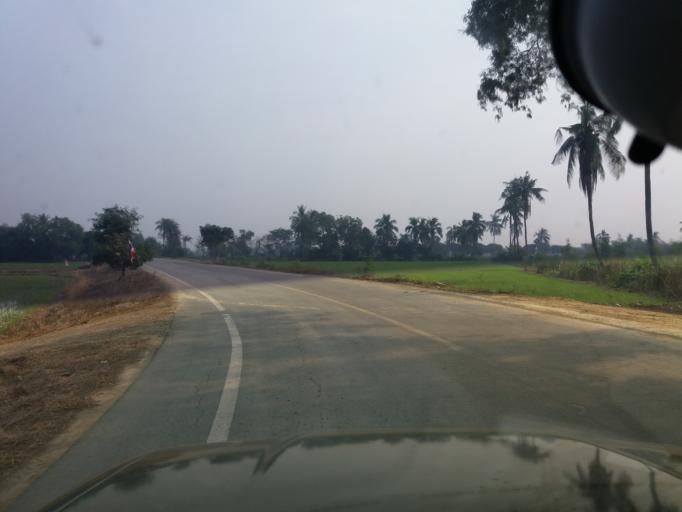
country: TH
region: Suphan Buri
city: Doem Bang Nang Buat
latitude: 14.8525
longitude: 100.1450
